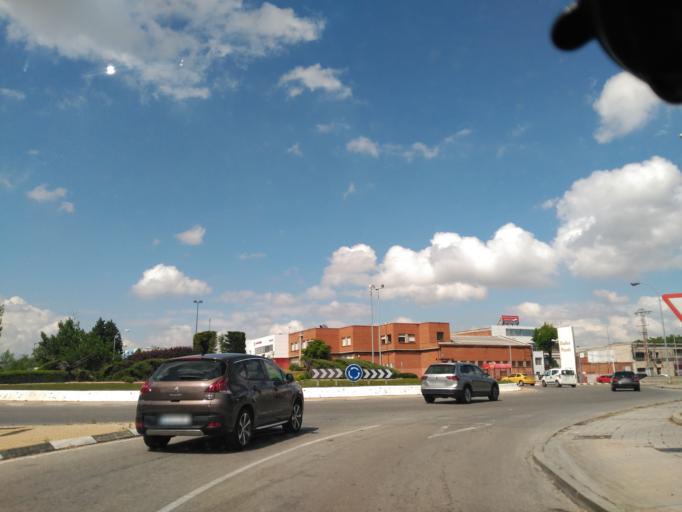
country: ES
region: Madrid
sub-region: Provincia de Madrid
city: Getafe
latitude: 40.3039
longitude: -3.7020
